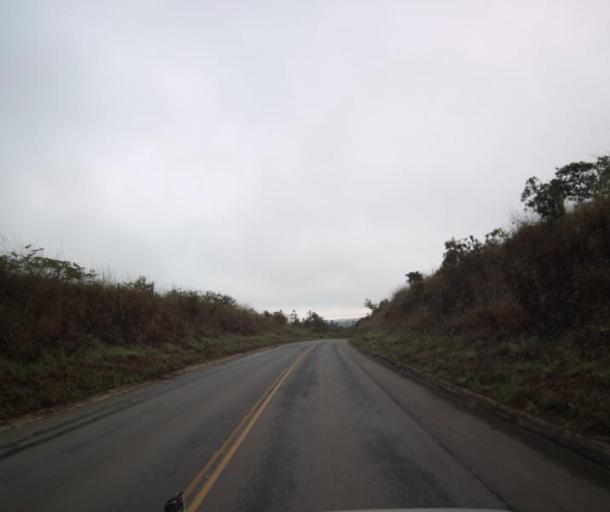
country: BR
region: Goias
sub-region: Pirenopolis
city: Pirenopolis
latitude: -15.8075
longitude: -48.7820
